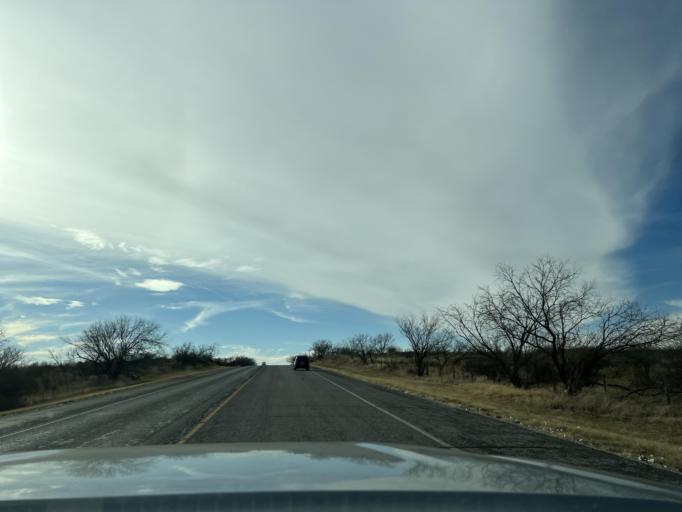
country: US
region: Texas
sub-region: Fisher County
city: Roby
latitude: 32.7571
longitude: -100.3250
